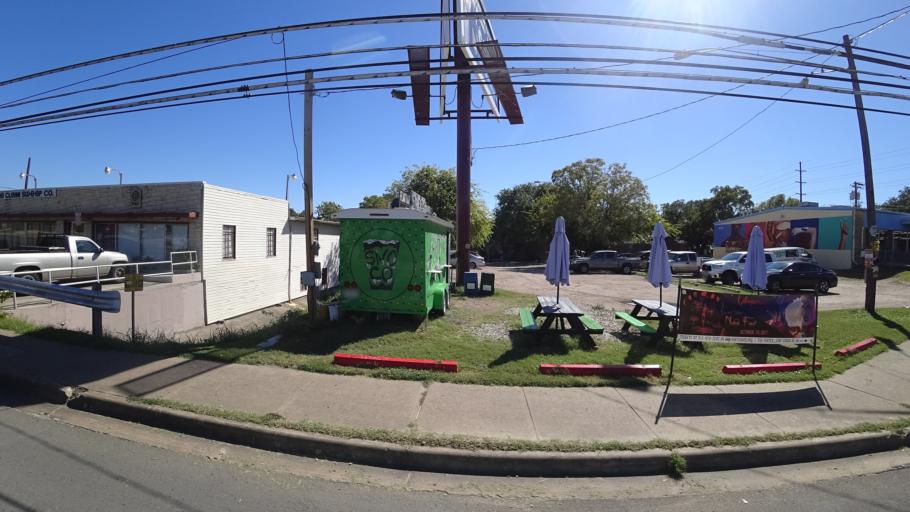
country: US
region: Texas
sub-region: Travis County
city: Austin
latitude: 30.2845
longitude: -97.7181
